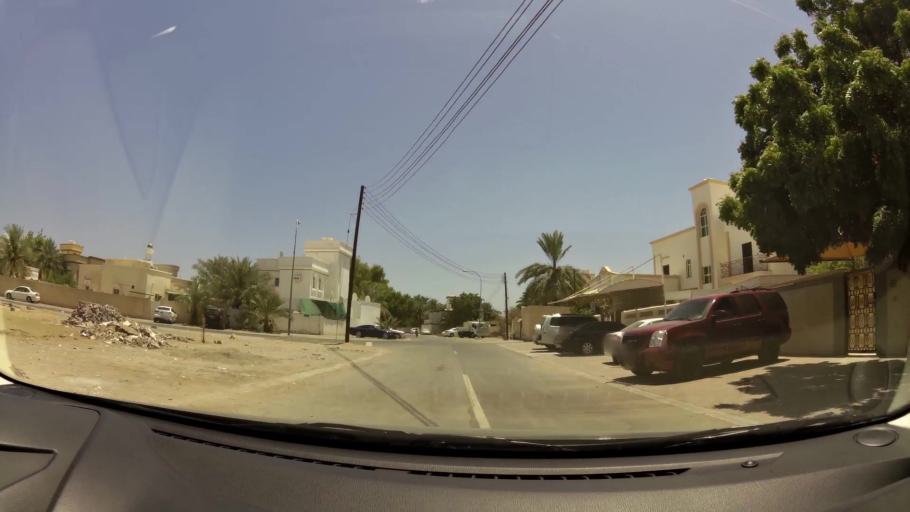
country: OM
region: Muhafazat Masqat
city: As Sib al Jadidah
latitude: 23.6245
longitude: 58.2438
